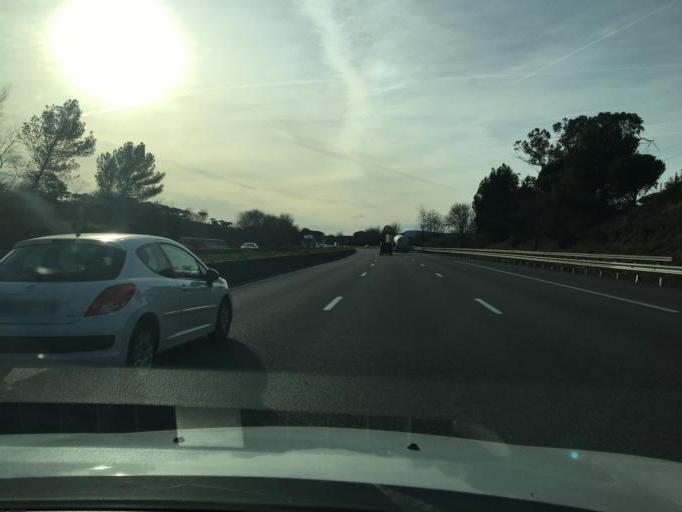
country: FR
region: Provence-Alpes-Cote d'Azur
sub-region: Departement du Var
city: Le Muy
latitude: 43.4646
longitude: 6.5721
